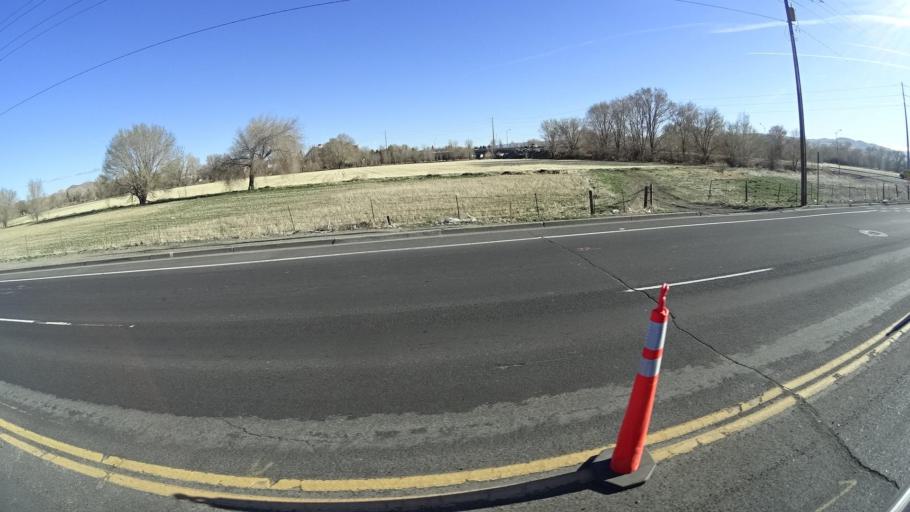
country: US
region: Nevada
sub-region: Washoe County
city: Sparks
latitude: 39.5162
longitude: -119.7629
